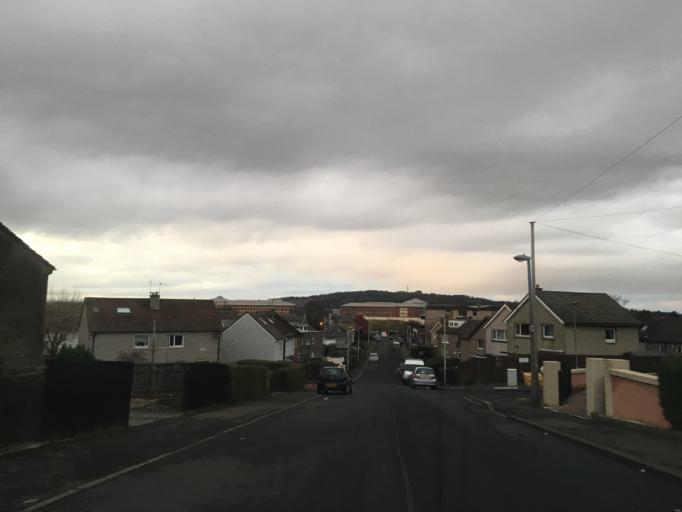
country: GB
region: Scotland
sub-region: Edinburgh
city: Colinton
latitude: 55.9228
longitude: -3.2589
